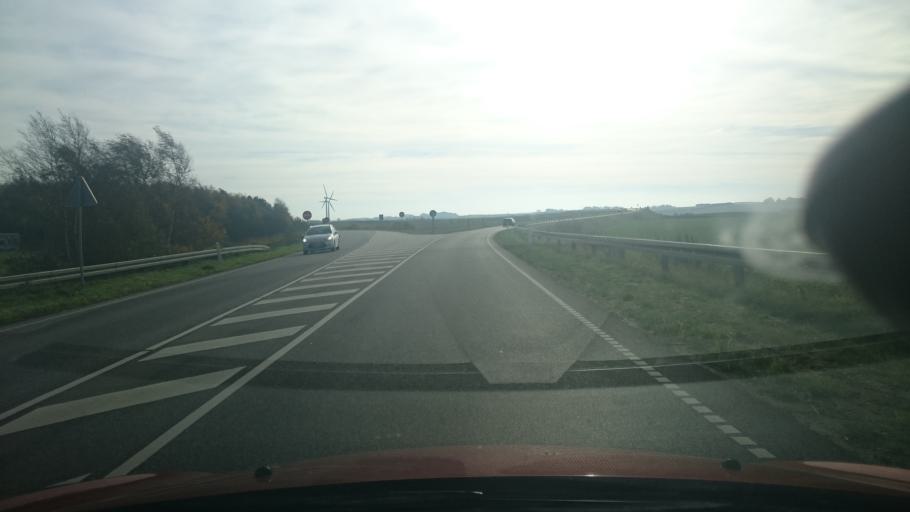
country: DK
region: Central Jutland
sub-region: Randers Kommune
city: Assentoft
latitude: 56.4342
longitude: 10.1322
